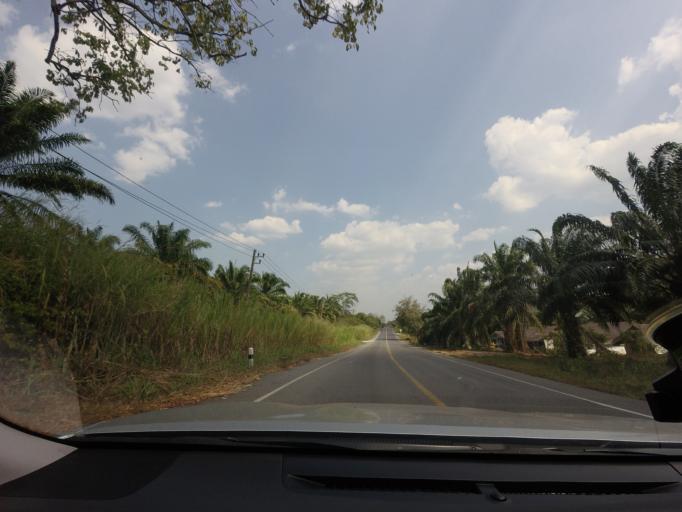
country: TH
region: Phangnga
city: Thap Put
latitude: 8.5332
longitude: 98.6235
